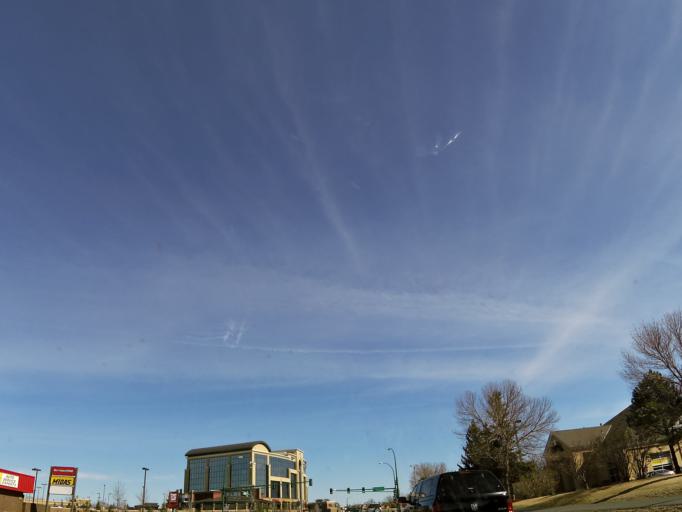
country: US
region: Minnesota
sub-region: Hennepin County
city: Eden Prairie
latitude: 44.8539
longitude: -93.4301
